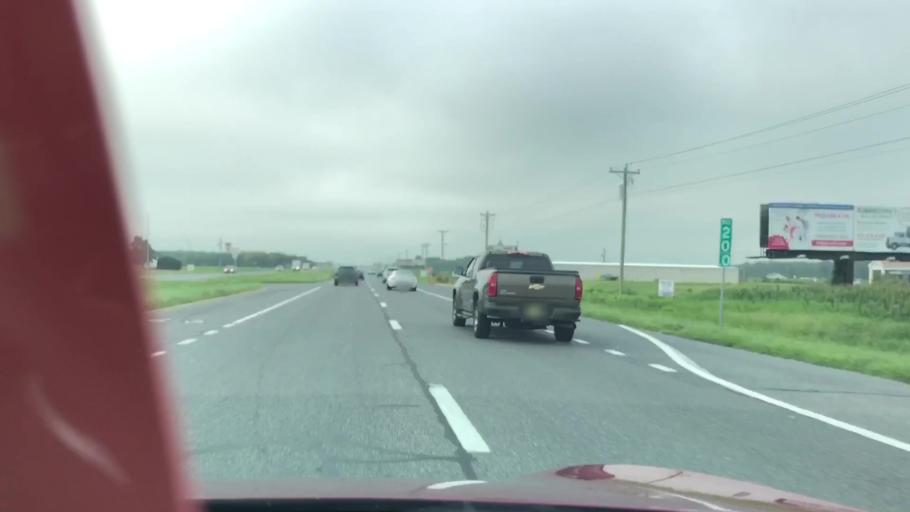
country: US
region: Delaware
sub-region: Sussex County
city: Bridgeville
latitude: 38.7378
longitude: -75.5921
